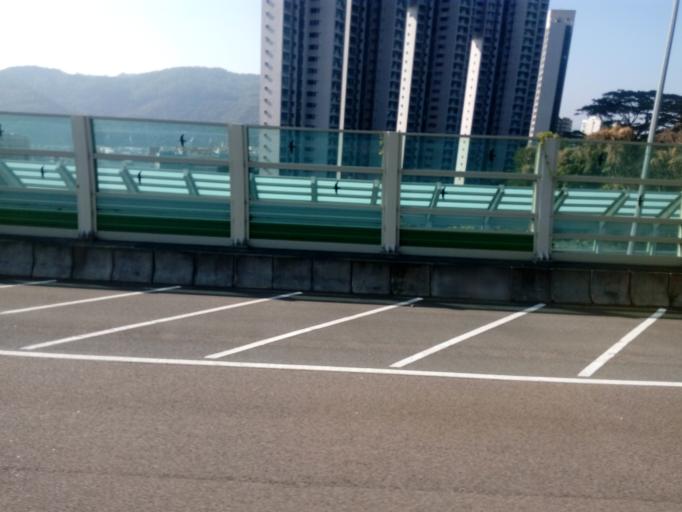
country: HK
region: Tsuen Wan
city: Tsuen Wan
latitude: 22.3708
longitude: 114.0933
